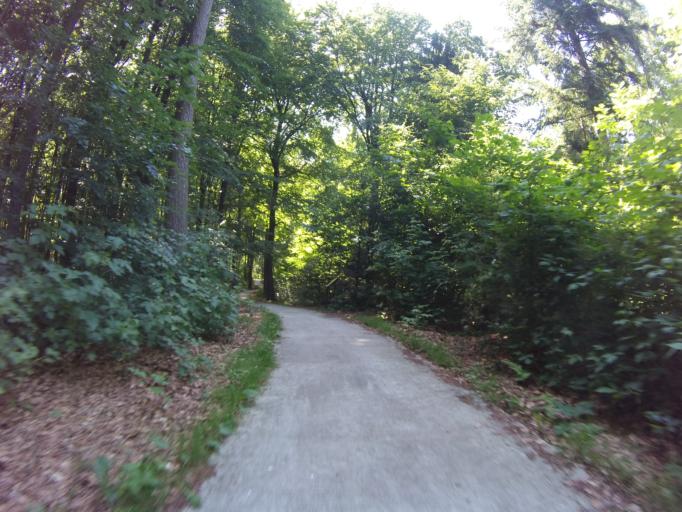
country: NL
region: Drenthe
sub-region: Gemeente Emmen
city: Emmen
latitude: 52.7894
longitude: 6.9169
